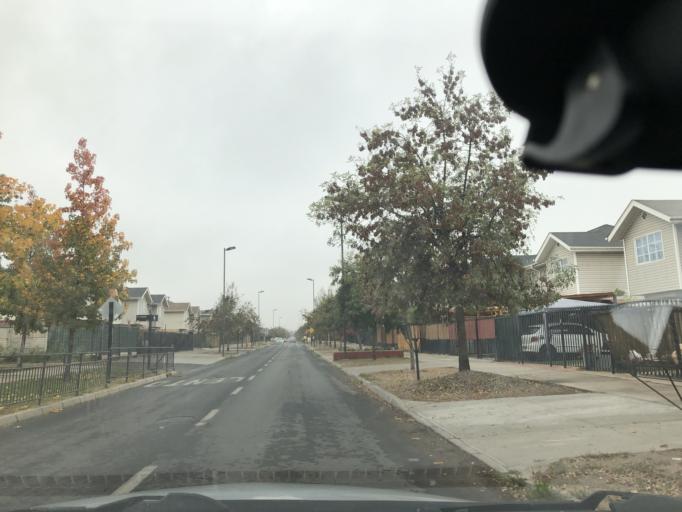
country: CL
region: Santiago Metropolitan
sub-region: Provincia de Cordillera
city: Puente Alto
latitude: -33.5929
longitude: -70.5923
